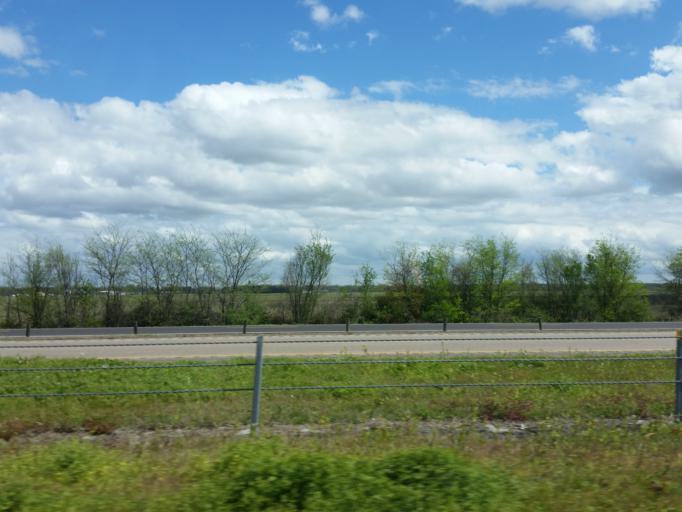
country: US
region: Arkansas
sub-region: Crittenden County
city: Marion
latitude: 35.3735
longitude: -90.2797
